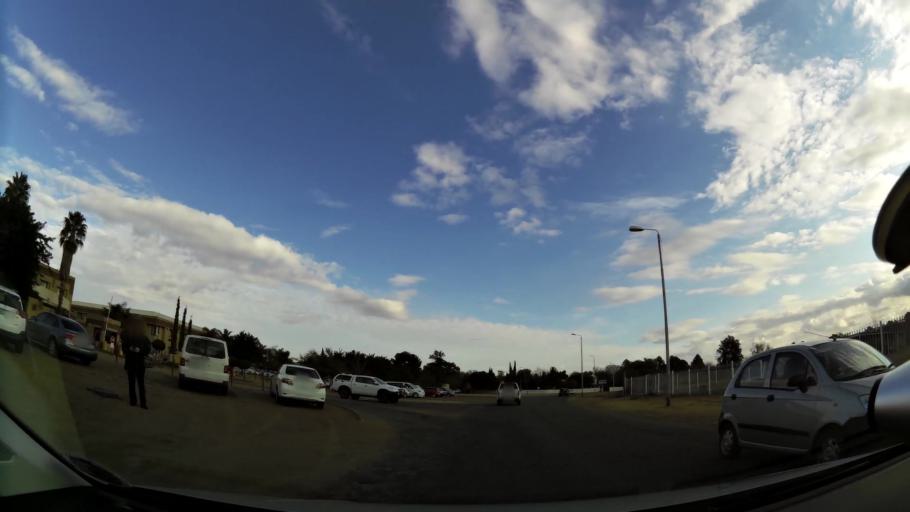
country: ZA
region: Orange Free State
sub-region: Lejweleputswa District Municipality
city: Welkom
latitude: -27.9876
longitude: 26.7296
